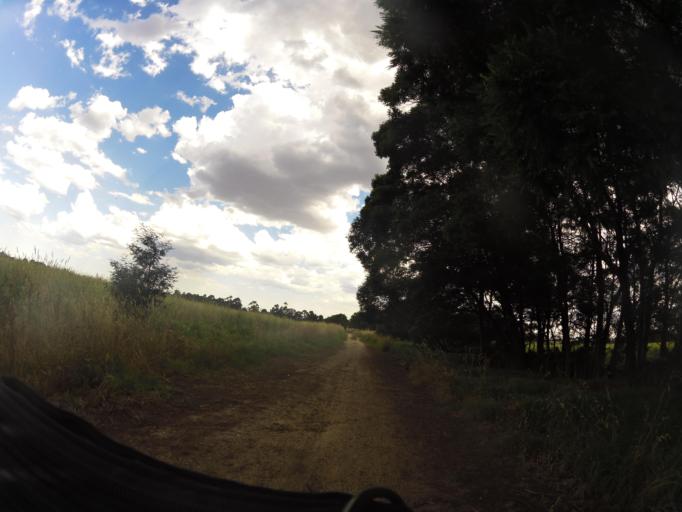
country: AU
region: Victoria
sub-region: Wellington
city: Heyfield
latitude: -38.0064
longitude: 146.6973
